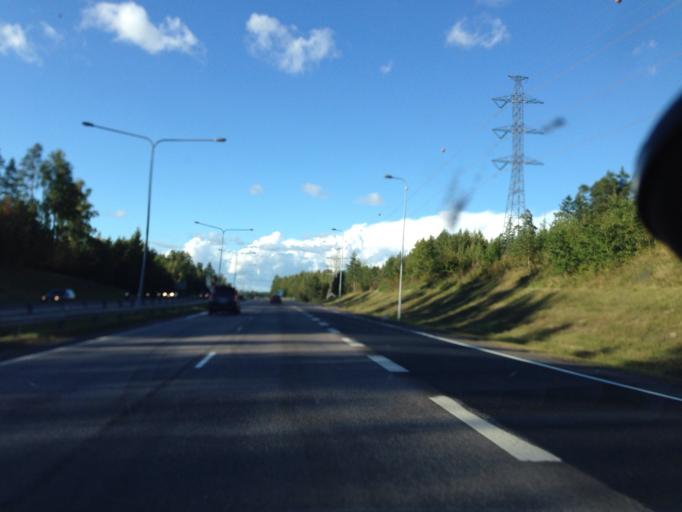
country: FI
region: Uusimaa
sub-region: Helsinki
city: Vantaa
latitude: 60.3265
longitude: 24.9984
